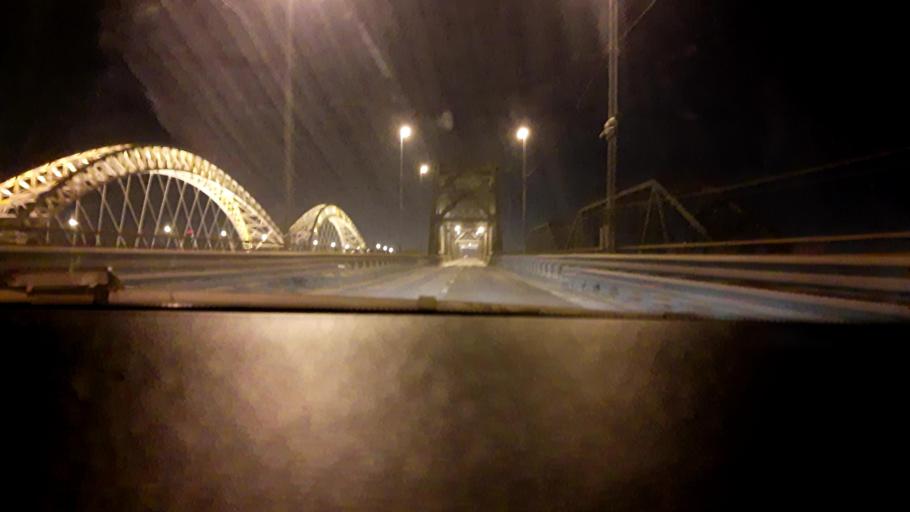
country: RU
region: Nizjnij Novgorod
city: Neklyudovo
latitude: 56.3553
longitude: 43.9256
